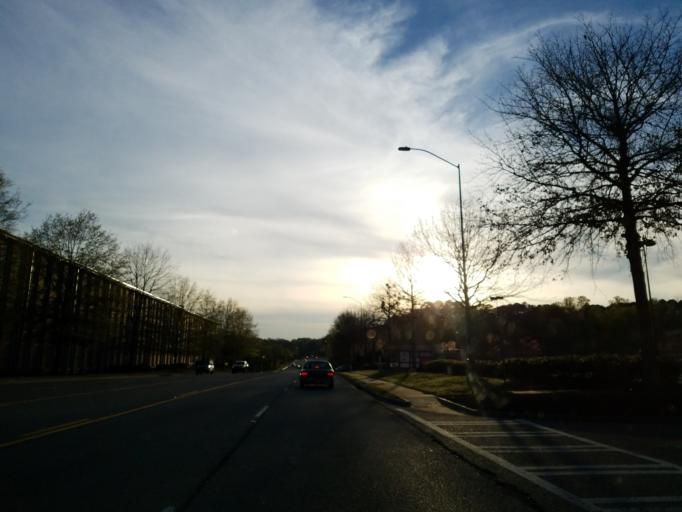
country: US
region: Georgia
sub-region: Cherokee County
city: Canton
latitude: 34.2451
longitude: -84.4845
